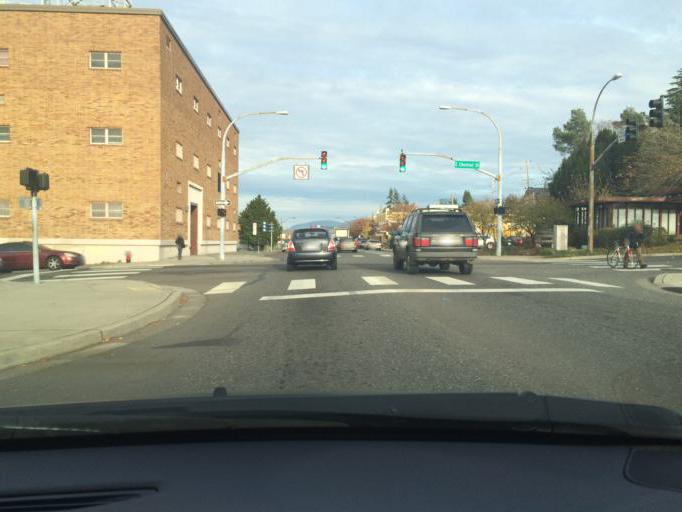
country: US
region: Washington
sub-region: Whatcom County
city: Bellingham
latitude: 48.7466
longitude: -122.4778
